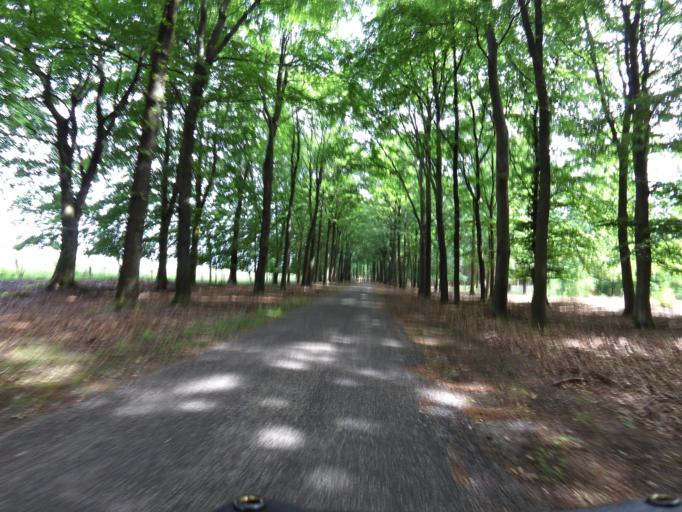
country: NL
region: Gelderland
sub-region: Gemeente Apeldoorn
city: Loenen
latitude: 52.0833
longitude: 5.9548
